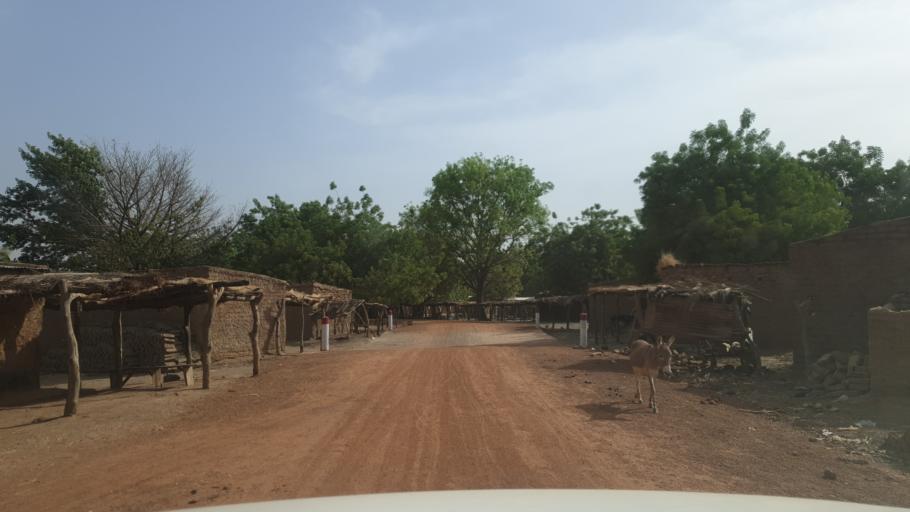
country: ML
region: Koulikoro
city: Kolokani
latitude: 13.3196
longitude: -8.2759
